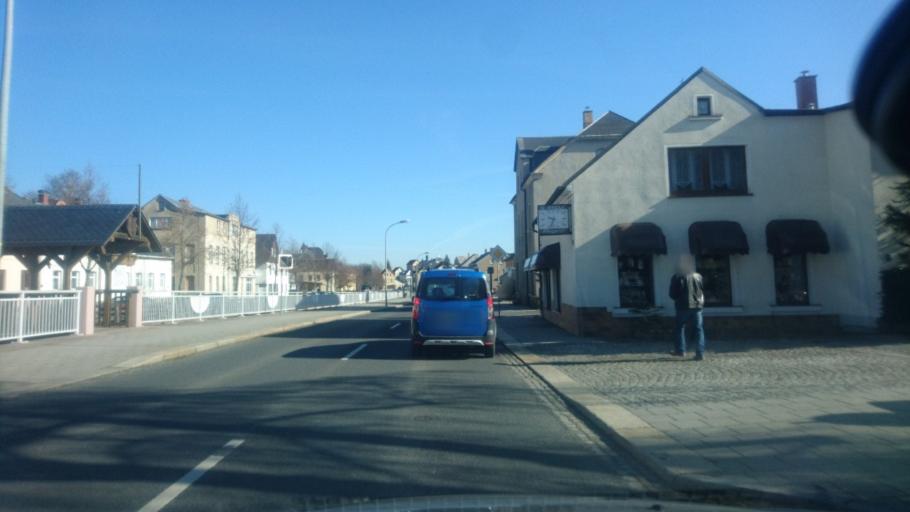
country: DE
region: Saxony
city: Ellefeld
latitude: 50.4857
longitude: 12.3910
